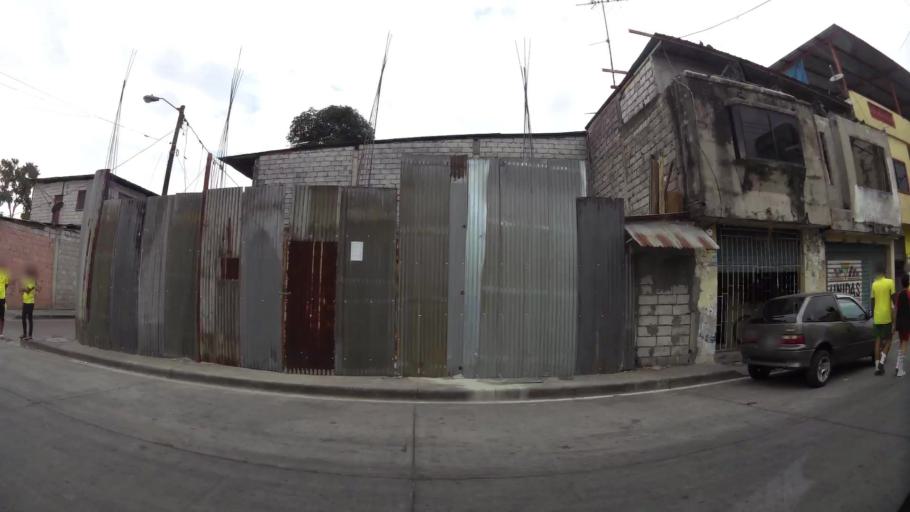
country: EC
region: Guayas
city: Guayaquil
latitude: -2.2548
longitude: -79.8775
